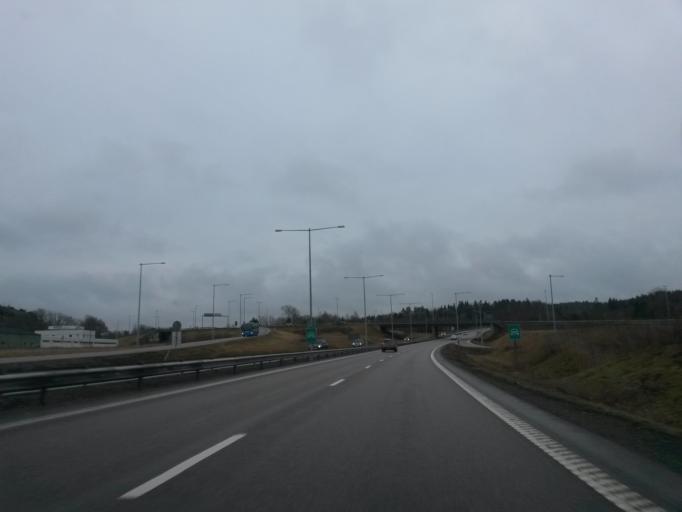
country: SE
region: Vaestra Goetaland
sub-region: Uddevalla Kommun
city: Uddevalla
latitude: 58.3502
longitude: 11.9808
